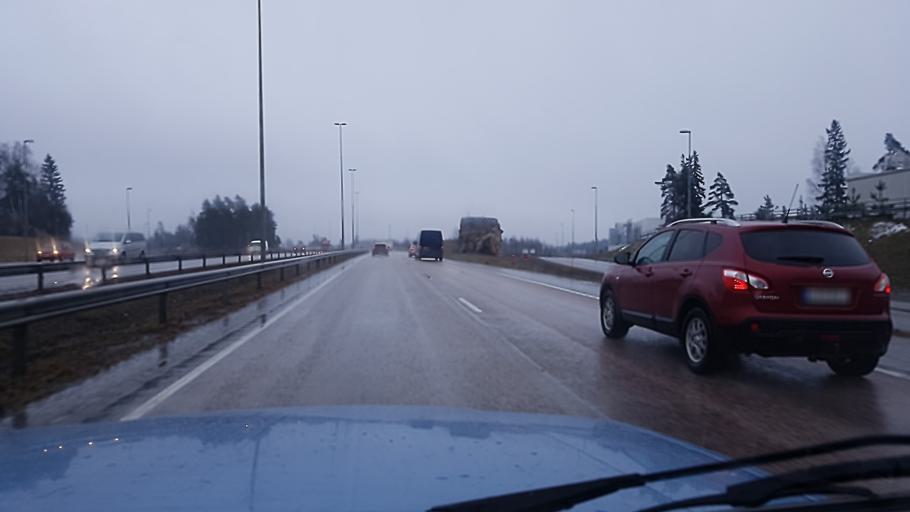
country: FI
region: Uusimaa
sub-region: Helsinki
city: Vantaa
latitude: 60.2977
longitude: 24.9107
